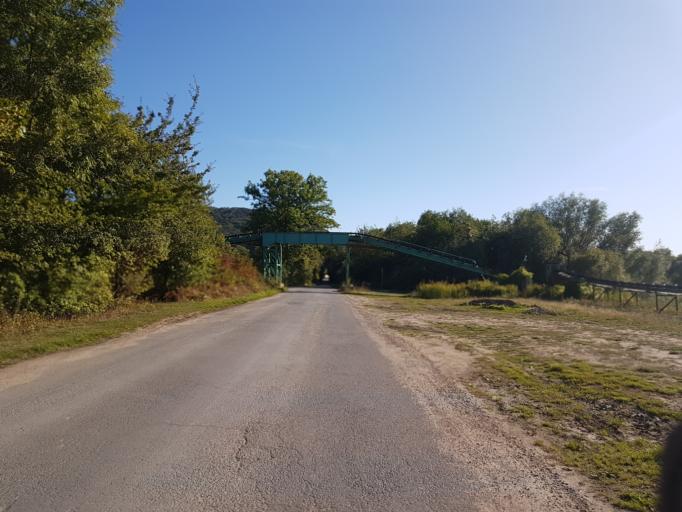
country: DE
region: North Rhine-Westphalia
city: Porta Westfalica
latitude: 52.2560
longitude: 8.9228
